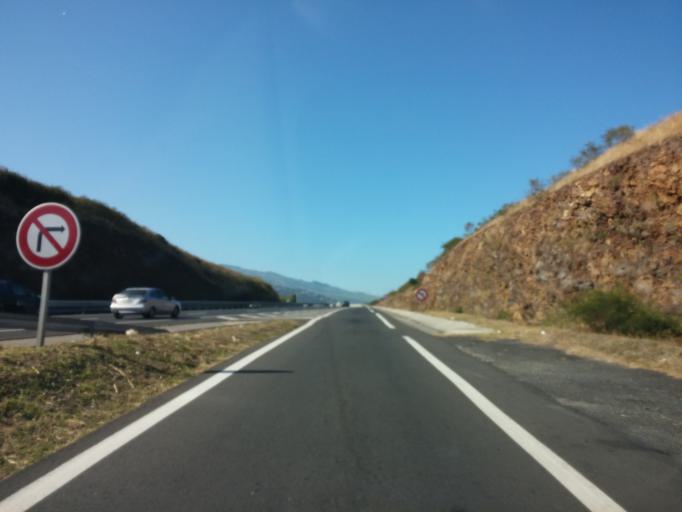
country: RE
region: Reunion
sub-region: Reunion
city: Trois-Bassins
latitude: -21.0902
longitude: 55.2568
